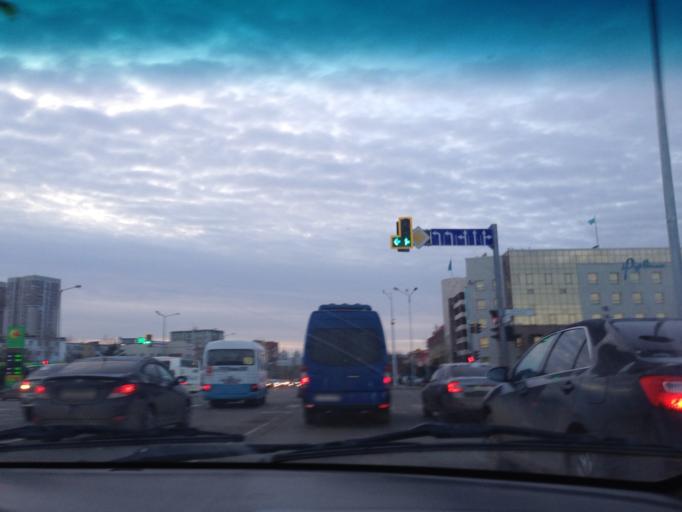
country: KZ
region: Astana Qalasy
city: Astana
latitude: 51.1517
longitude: 71.4558
